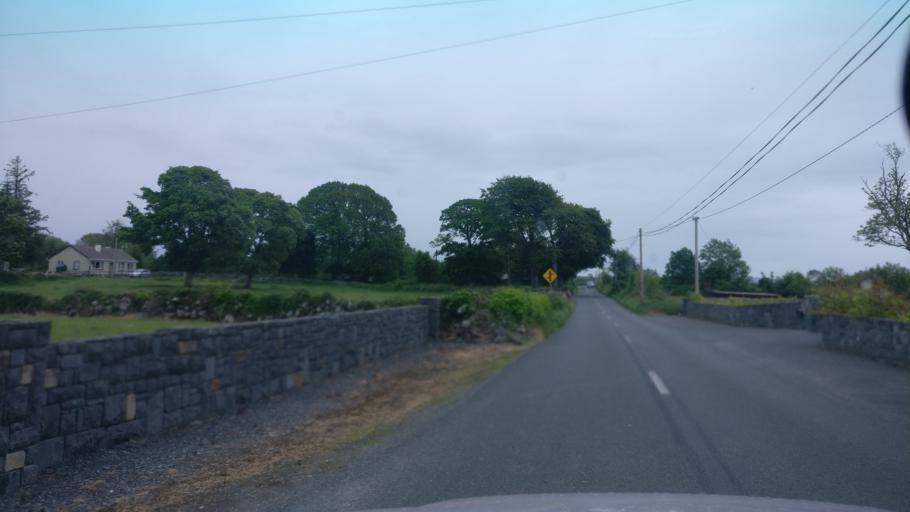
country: IE
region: Connaught
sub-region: County Galway
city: Gort
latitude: 53.0667
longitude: -8.7781
